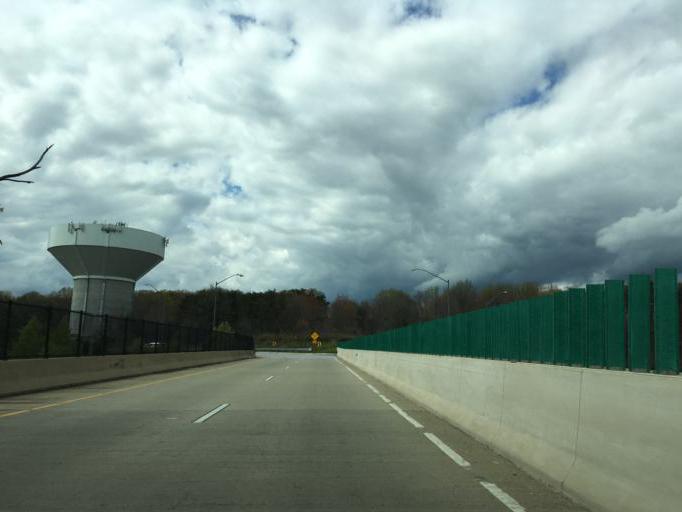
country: US
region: Maryland
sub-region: Anne Arundel County
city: Jessup
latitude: 39.1561
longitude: -76.7451
